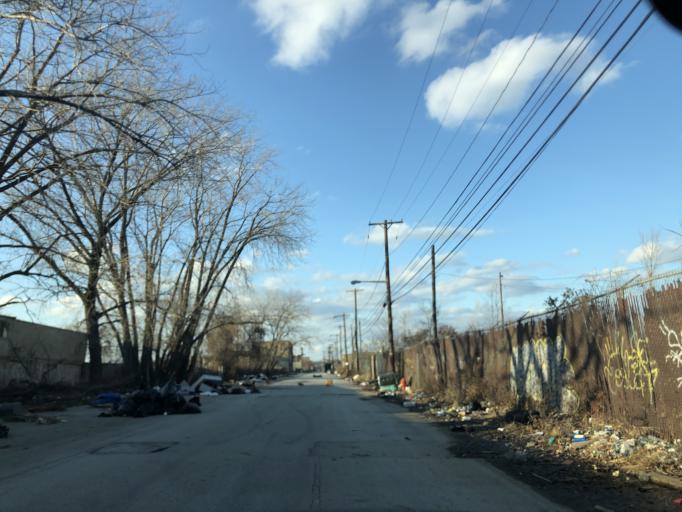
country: US
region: New Jersey
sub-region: Camden County
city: Pennsauken
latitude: 39.9815
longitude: -75.0898
